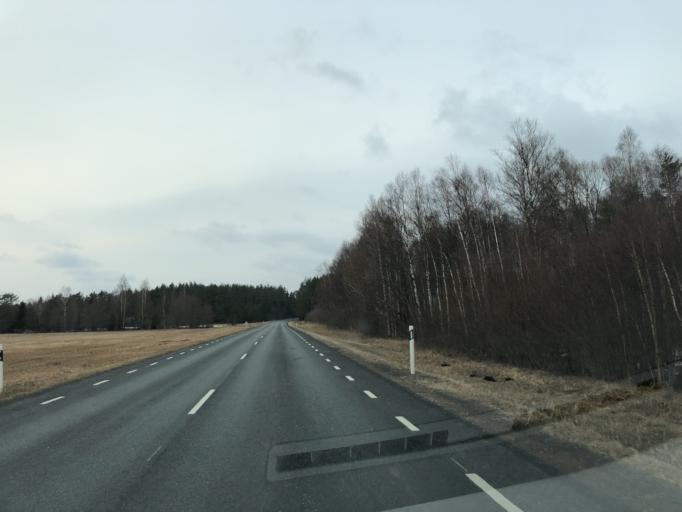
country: EE
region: Viljandimaa
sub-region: Suure-Jaani vald
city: Suure-Jaani
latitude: 58.5683
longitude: 25.3960
